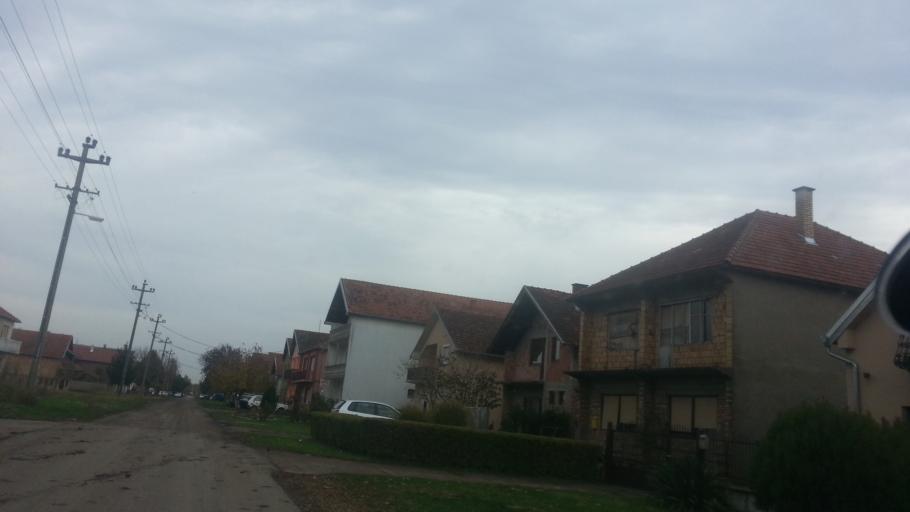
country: RS
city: Golubinci
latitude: 44.9833
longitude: 20.0511
